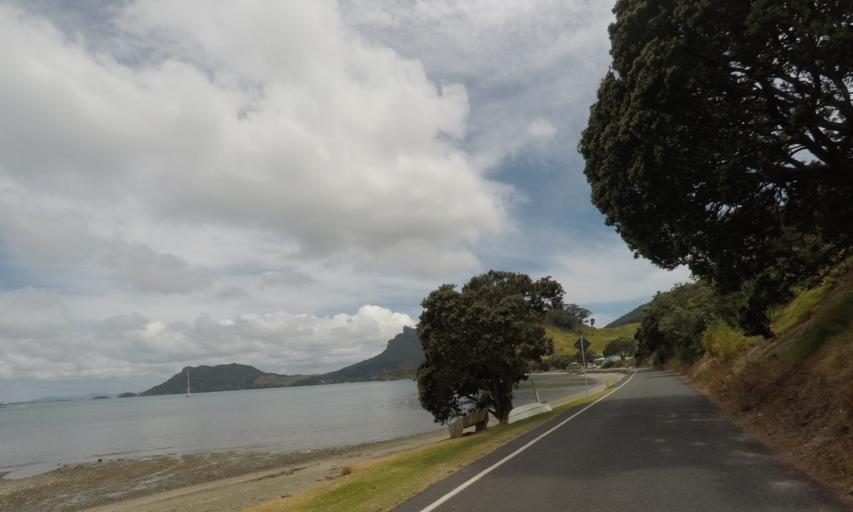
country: NZ
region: Northland
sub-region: Whangarei
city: Ruakaka
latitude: -35.8440
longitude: 174.5368
